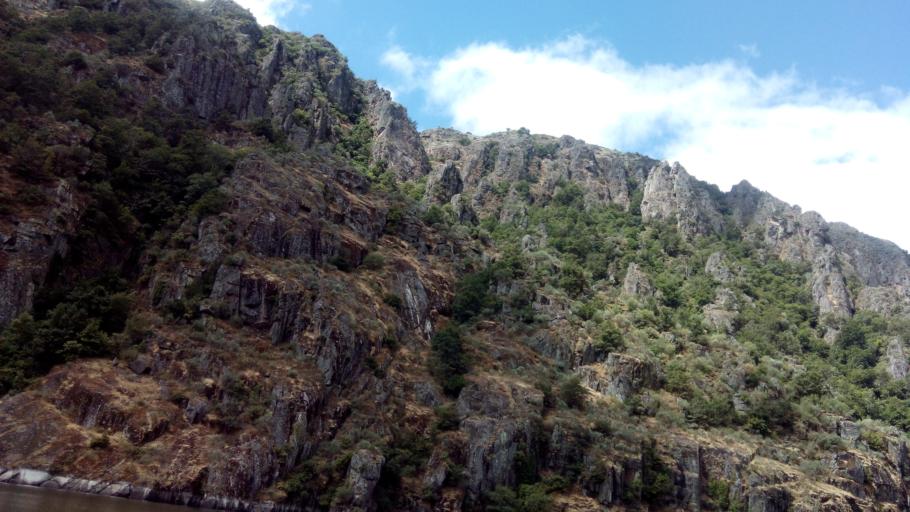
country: ES
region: Galicia
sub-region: Provincia de Lugo
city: Sober
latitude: 42.3858
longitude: -7.6192
